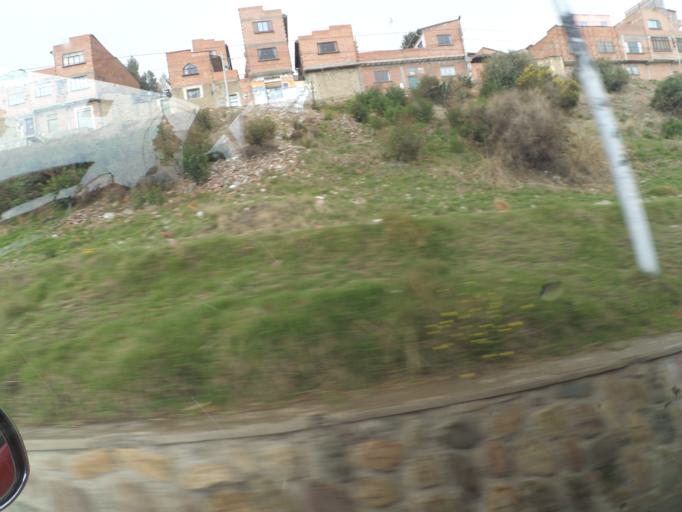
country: BO
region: La Paz
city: La Paz
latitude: -16.4919
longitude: -68.1682
